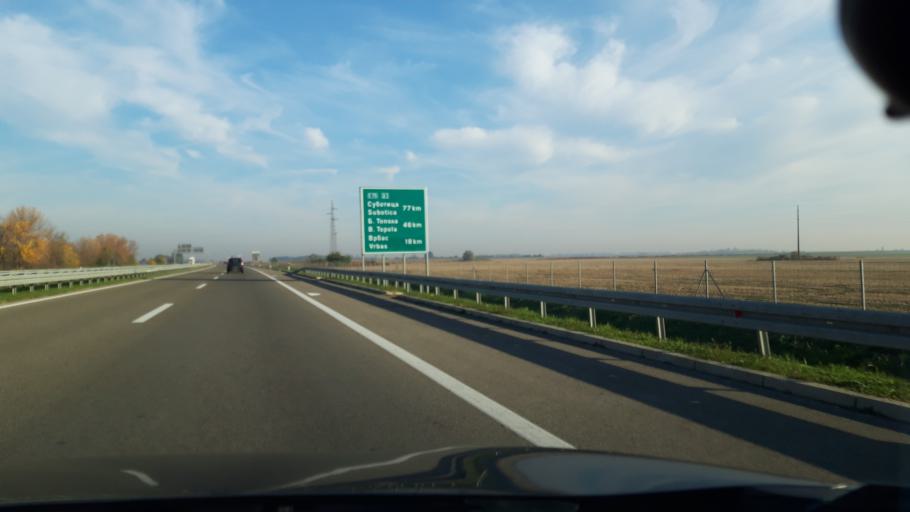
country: RS
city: Zmajevo
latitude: 45.4437
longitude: 19.7372
